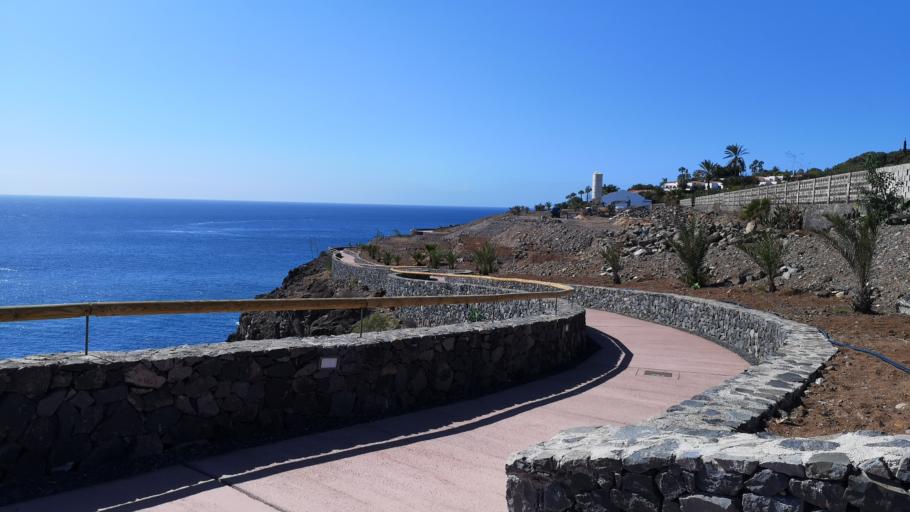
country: ES
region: Canary Islands
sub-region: Provincia de Santa Cruz de Tenerife
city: Alajero
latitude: 28.0321
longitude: -17.1837
